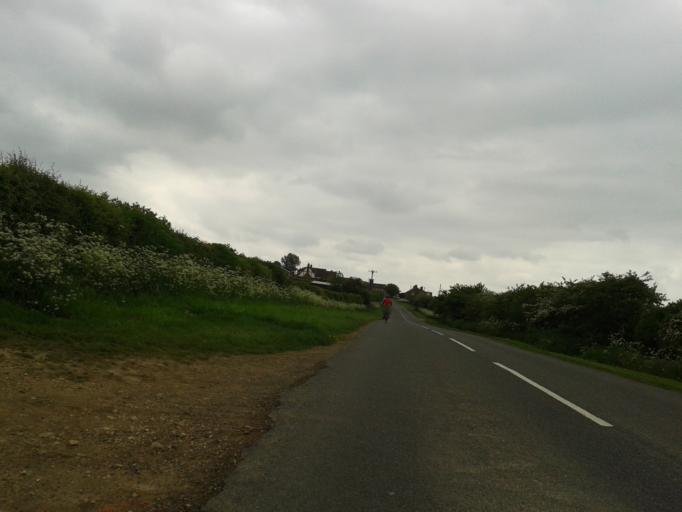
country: GB
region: England
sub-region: Northamptonshire
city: Corby
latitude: 52.5073
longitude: -0.7485
